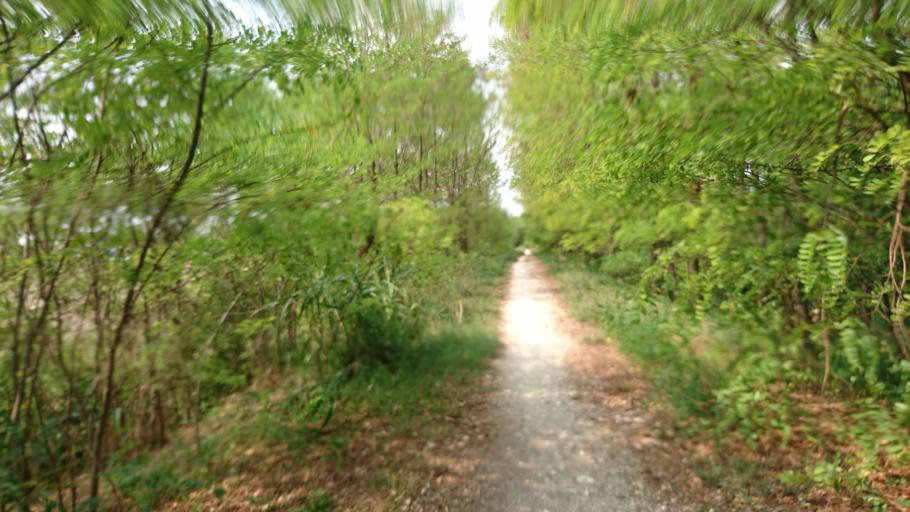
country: IT
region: Veneto
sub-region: Provincia di Padova
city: Saletto
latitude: 45.4694
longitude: 11.8602
